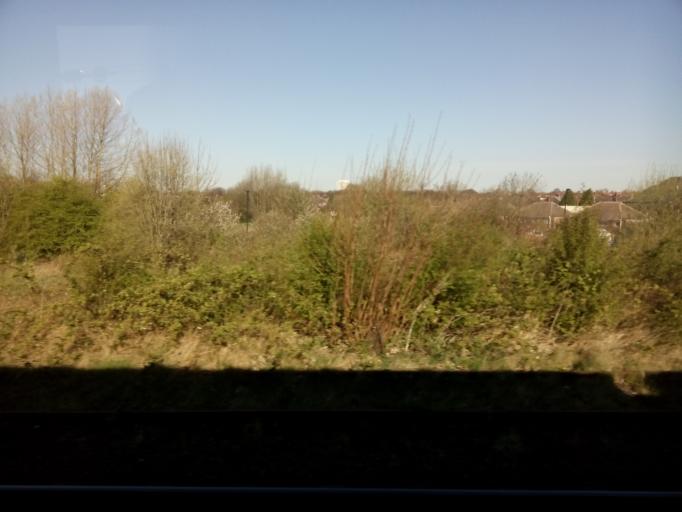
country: GB
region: England
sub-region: Borough of North Tyneside
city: Wallsend
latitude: 54.9901
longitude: -1.5642
